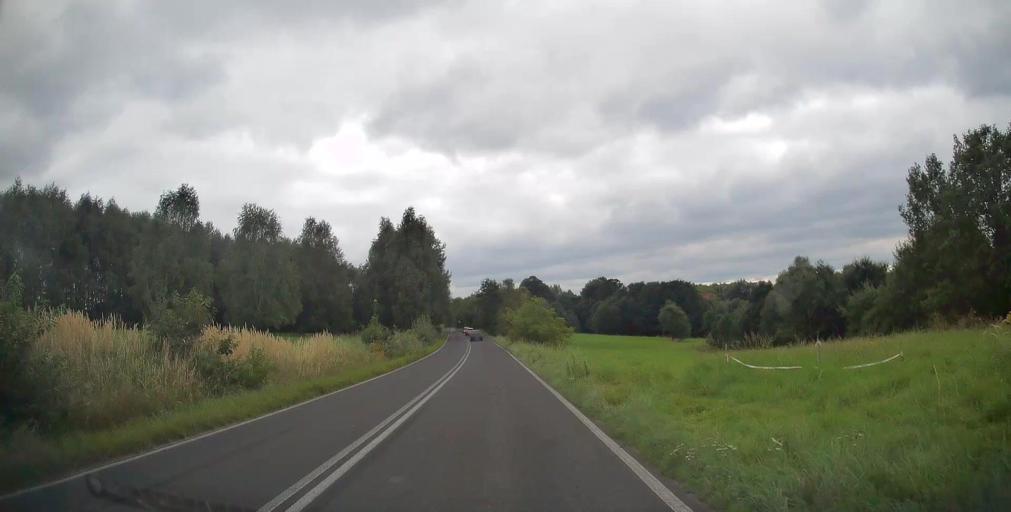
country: PL
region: Lesser Poland Voivodeship
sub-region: Powiat chrzanowski
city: Grojec
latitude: 50.0825
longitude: 19.5546
